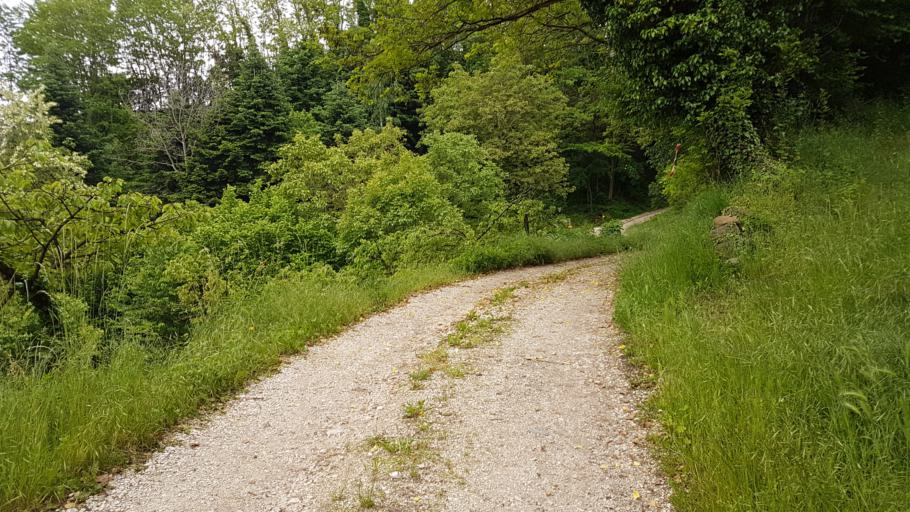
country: IT
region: Veneto
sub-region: Provincia di Vicenza
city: Nogarole Vicentino
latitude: 45.5501
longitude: 11.3150
